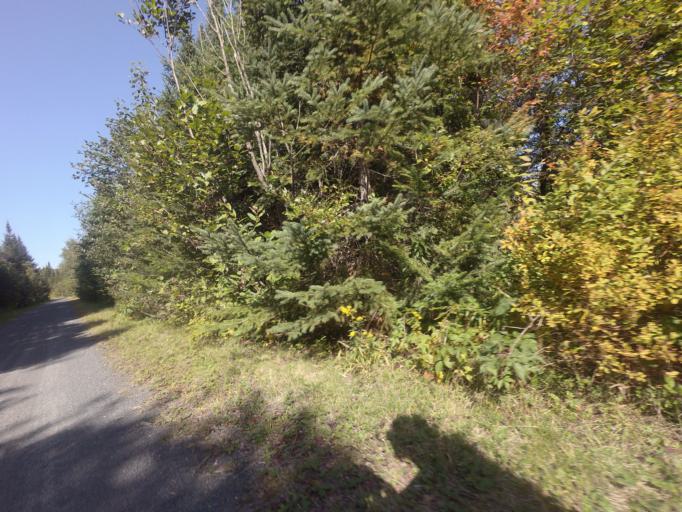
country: CA
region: Quebec
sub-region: Laurentides
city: Sainte-Agathe-des-Monts
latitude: 46.0829
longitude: -74.3337
